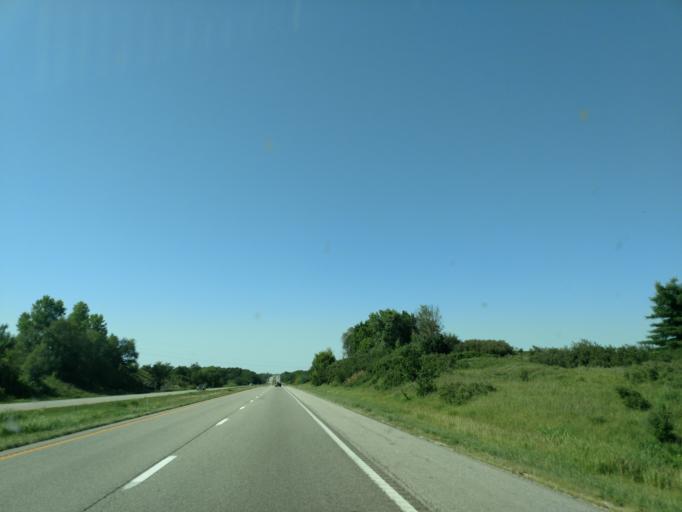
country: US
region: Missouri
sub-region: Platte County
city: Weston
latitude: 39.5568
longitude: -94.7879
